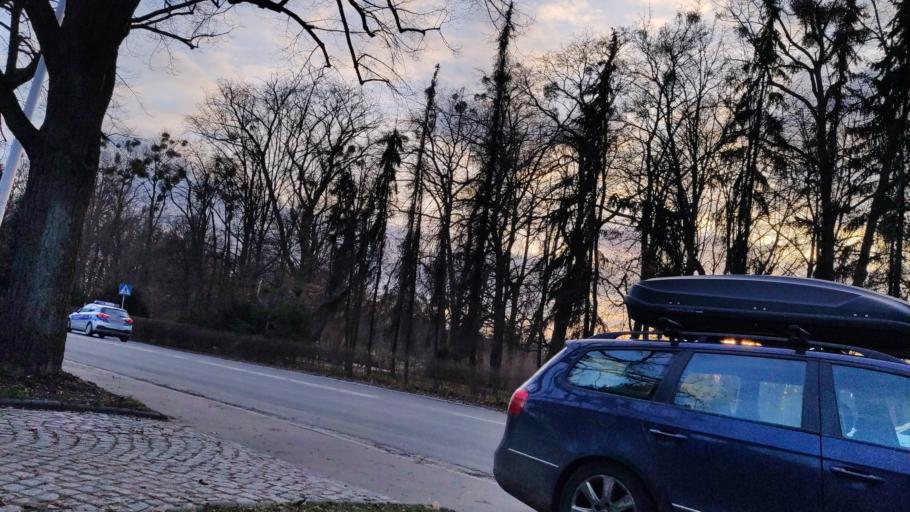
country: PL
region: Lower Silesian Voivodeship
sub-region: Powiat wroclawski
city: Wroclaw
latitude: 51.0755
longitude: 17.0136
